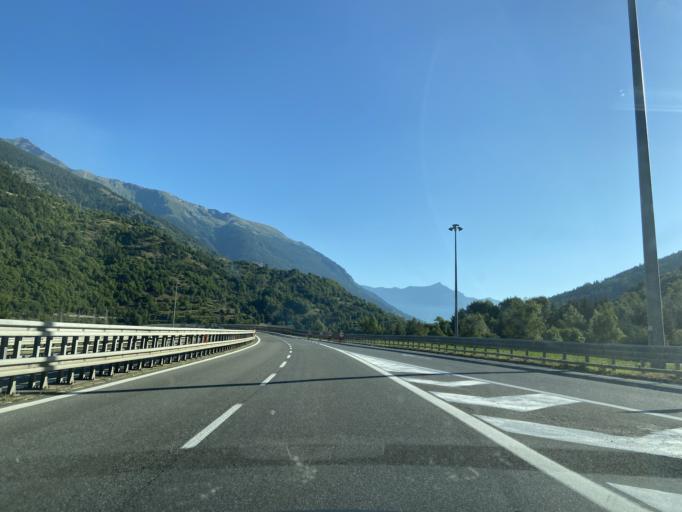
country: IT
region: Piedmont
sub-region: Provincia di Torino
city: Salbertrand
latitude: 45.0720
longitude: 6.8930
